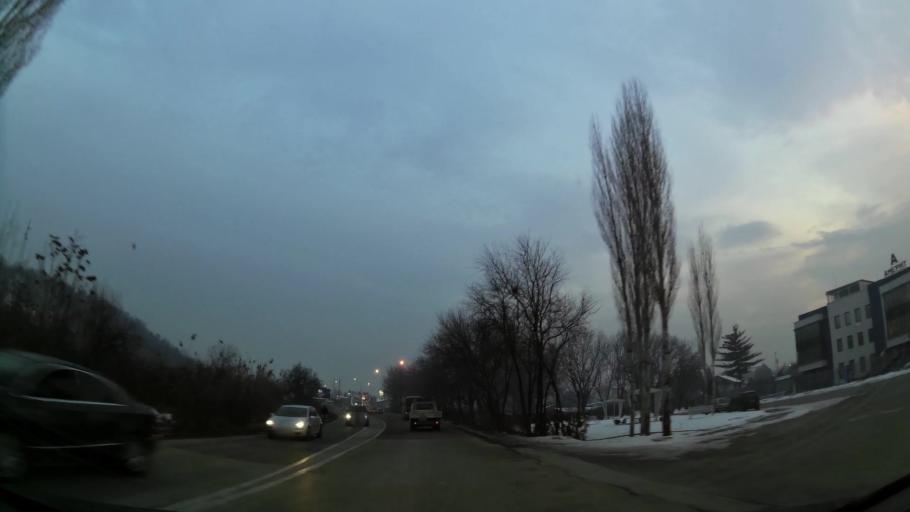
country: MK
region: Suto Orizari
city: Suto Orizare
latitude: 42.0173
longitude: 21.4107
